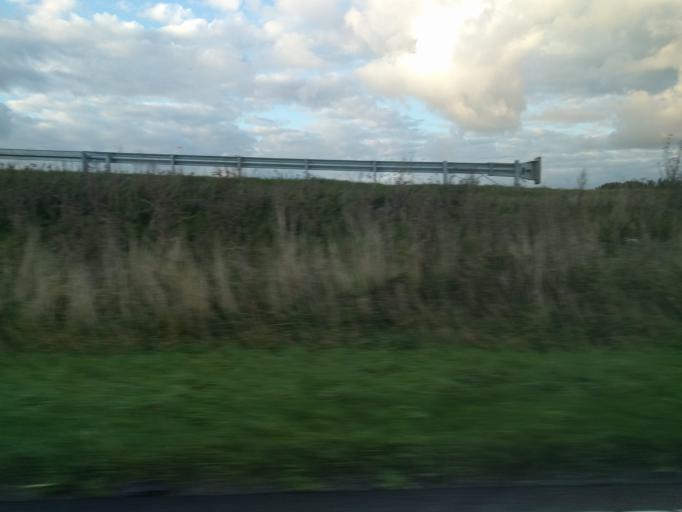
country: DK
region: Zealand
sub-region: Slagelse Kommune
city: Forlev
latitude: 55.3677
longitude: 11.2363
